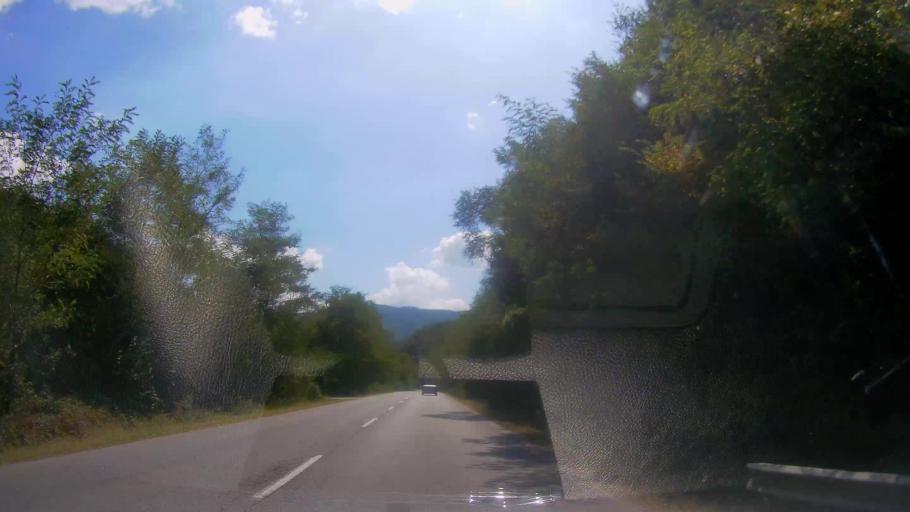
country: BG
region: Stara Zagora
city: Gurkovo
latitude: 42.7286
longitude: 25.7122
